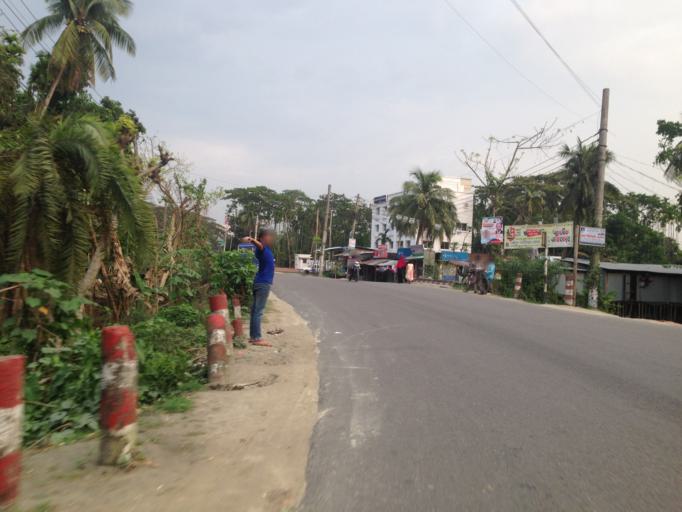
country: BD
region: Chittagong
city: Lakshmipur
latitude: 22.9468
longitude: 90.8087
